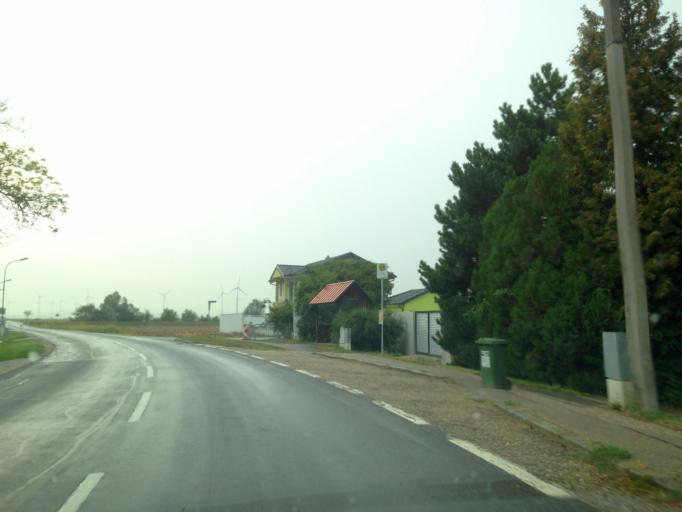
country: AT
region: Lower Austria
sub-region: Politischer Bezirk Bruck an der Leitha
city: Rohrau
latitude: 48.0769
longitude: 16.8910
